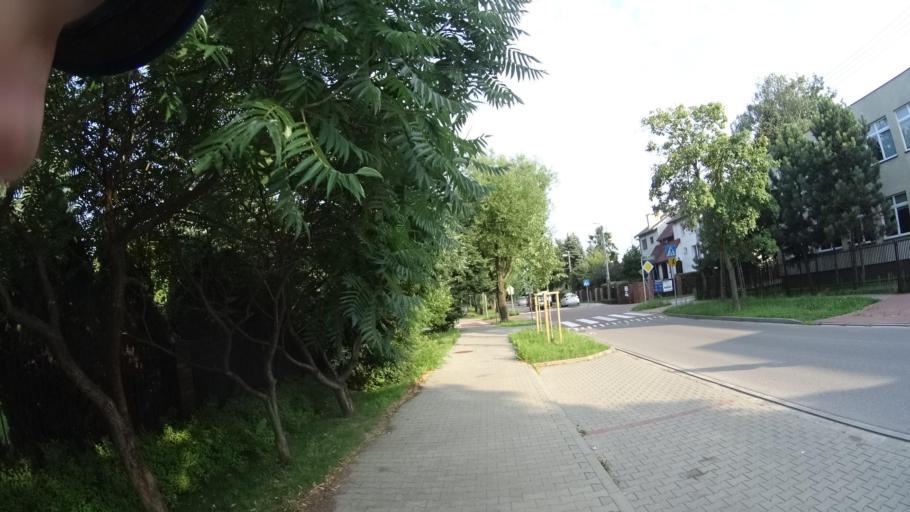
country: PL
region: Masovian Voivodeship
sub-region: Powiat pruszkowski
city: Michalowice
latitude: 52.1682
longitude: 20.8904
